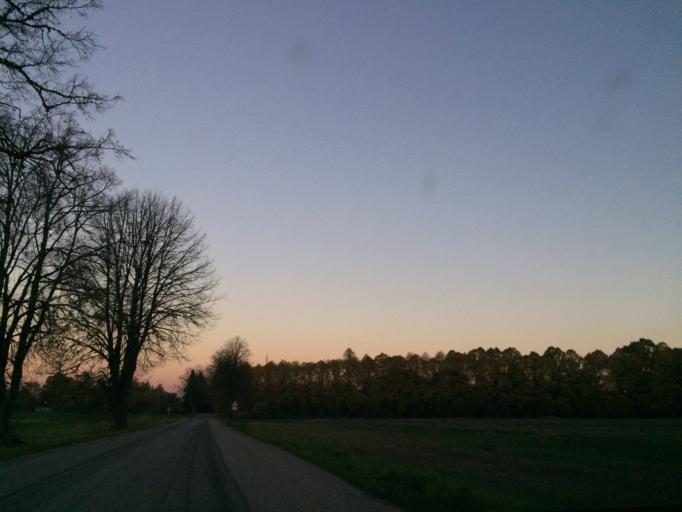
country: LT
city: Vieksniai
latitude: 56.3890
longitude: 22.6022
